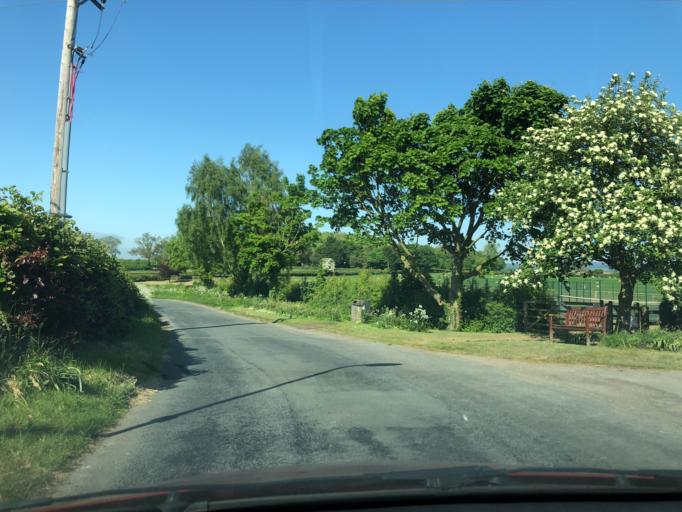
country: GB
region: England
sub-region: North Yorkshire
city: Northallerton
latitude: 54.3090
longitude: -1.3882
